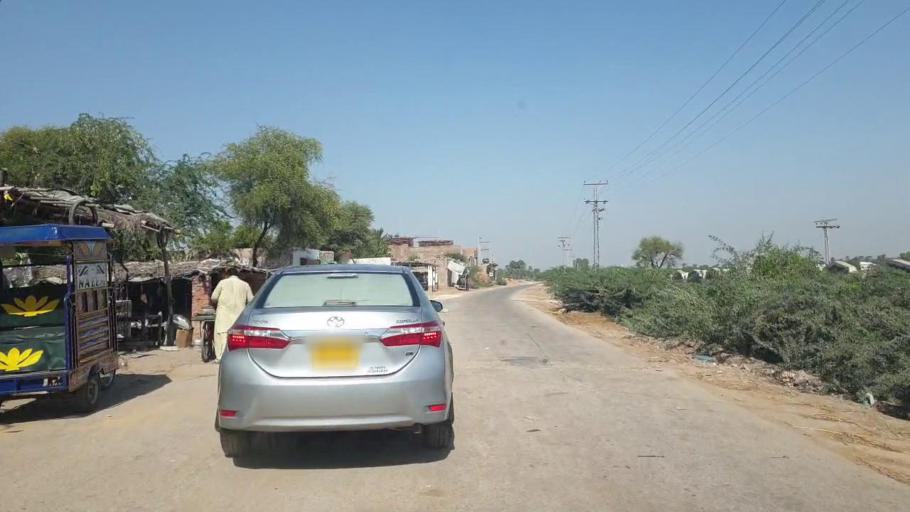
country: PK
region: Sindh
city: Talhar
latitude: 24.8867
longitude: 68.8205
